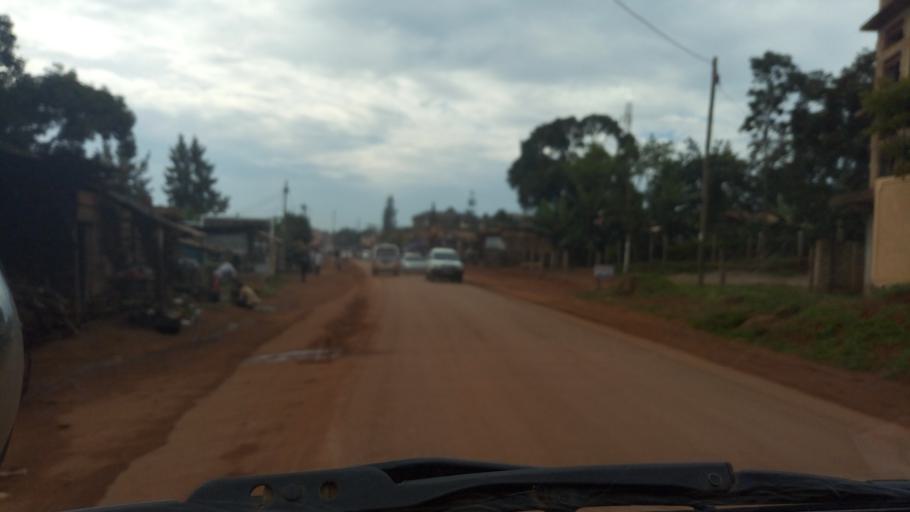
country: UG
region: Central Region
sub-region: Mukono District
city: Mukono
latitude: 0.3640
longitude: 32.7151
